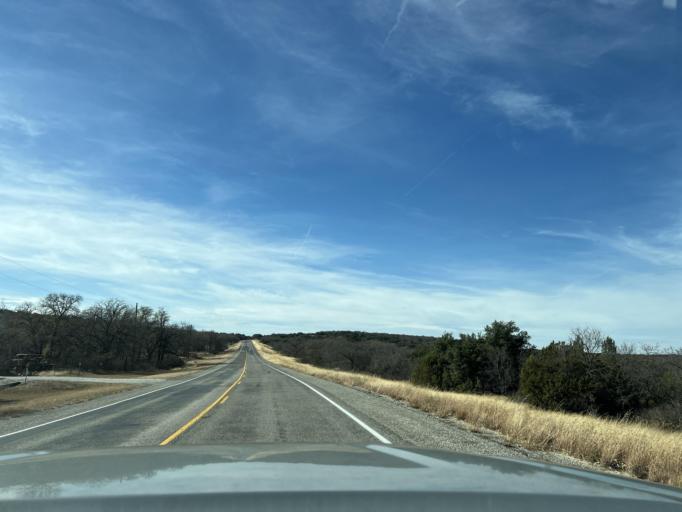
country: US
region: Texas
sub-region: Eastland County
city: Cisco
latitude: 32.4646
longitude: -99.0207
